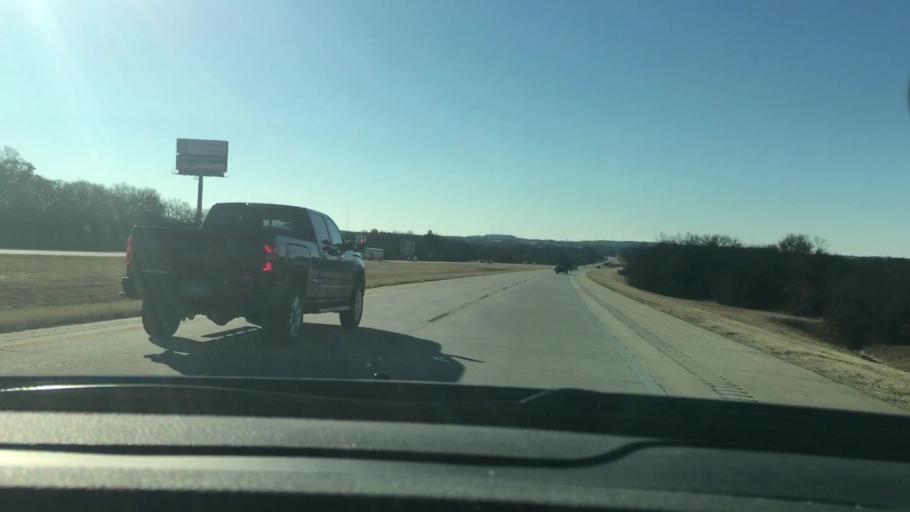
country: US
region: Oklahoma
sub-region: Carter County
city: Ardmore
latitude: 34.0549
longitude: -97.1490
